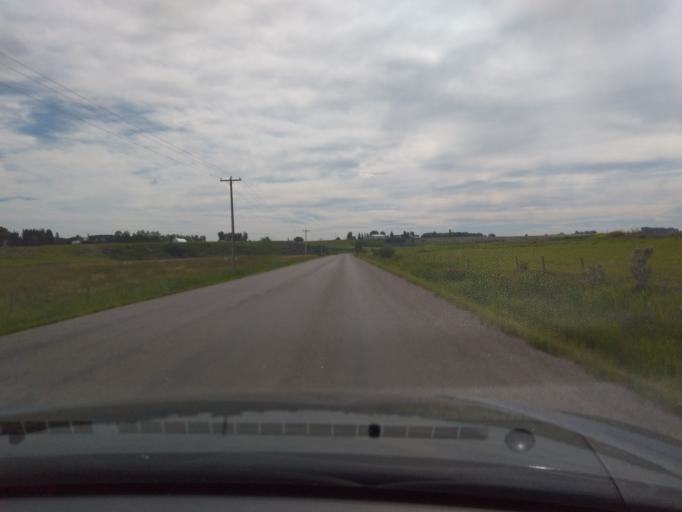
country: CA
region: Alberta
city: Didsbury
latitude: 51.6567
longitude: -114.1065
